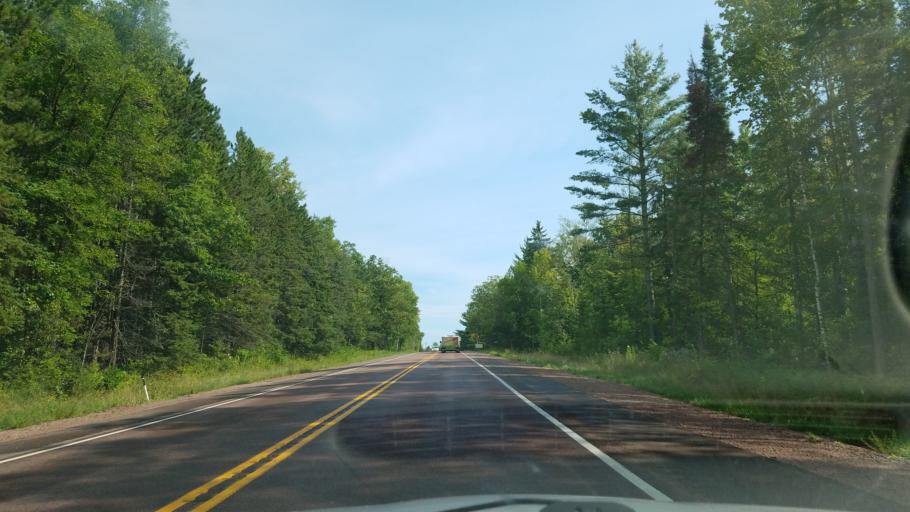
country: US
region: Wisconsin
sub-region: Ashland County
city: Ashland
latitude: 46.6041
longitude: -90.9513
